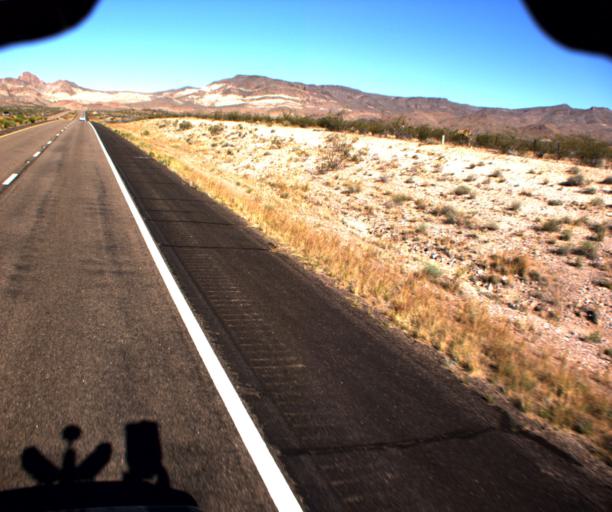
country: US
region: Arizona
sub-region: Mohave County
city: Golden Valley
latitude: 35.2282
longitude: -114.3418
